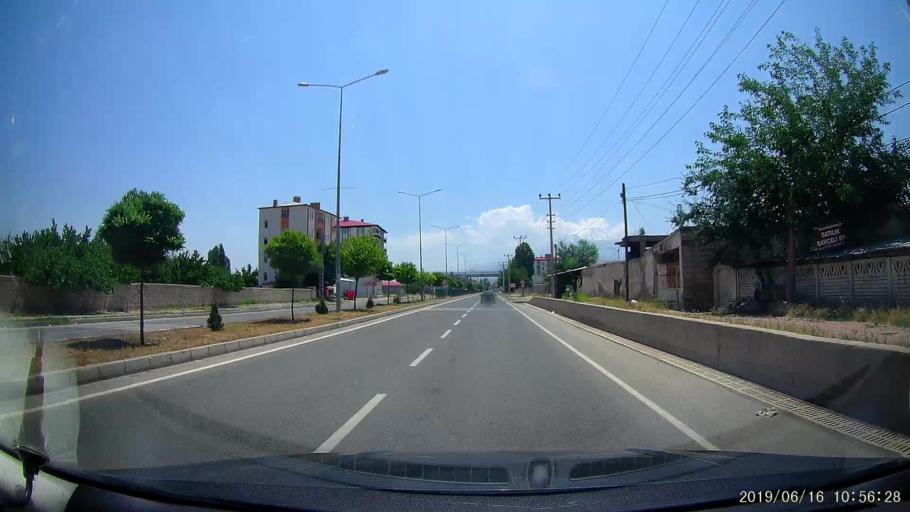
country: TR
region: Igdir
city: Igdir
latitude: 39.9295
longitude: 44.0228
